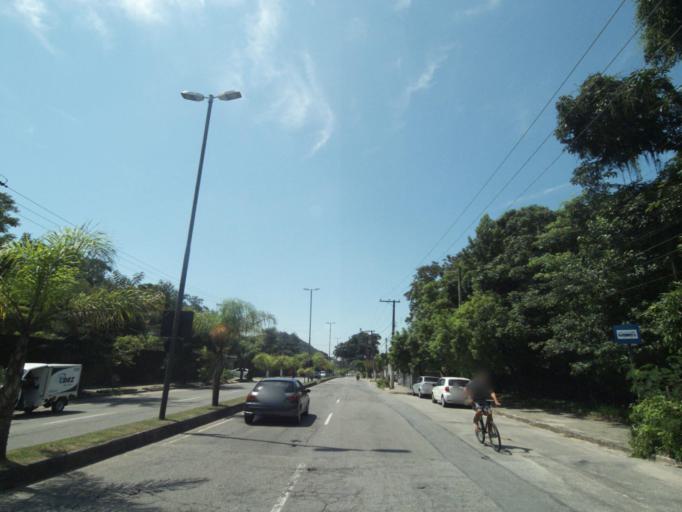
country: BR
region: Rio de Janeiro
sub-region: Niteroi
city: Niteroi
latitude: -22.9005
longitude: -43.0420
